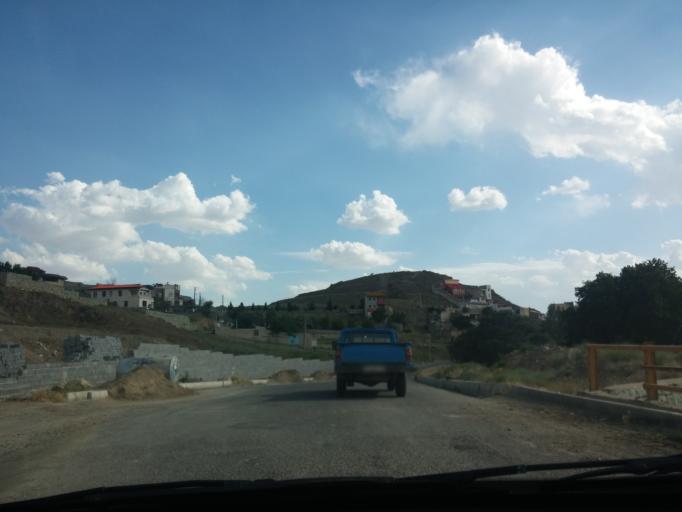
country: IR
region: Tehran
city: Damavand
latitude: 35.7294
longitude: 51.9060
